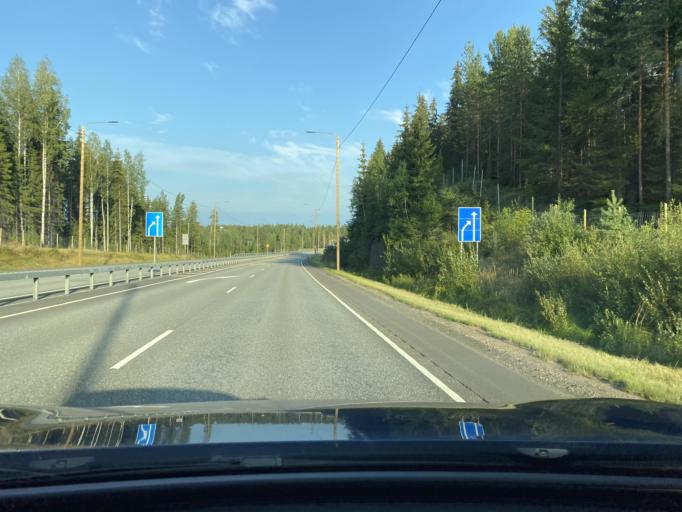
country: FI
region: Kymenlaakso
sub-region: Kouvola
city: Kouvola
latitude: 60.8686
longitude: 26.5428
